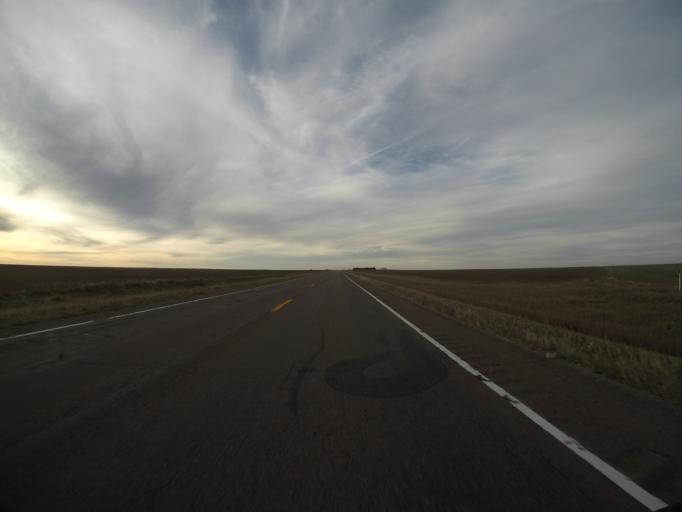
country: US
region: Colorado
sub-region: Yuma County
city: Yuma
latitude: 39.6786
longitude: -102.9634
